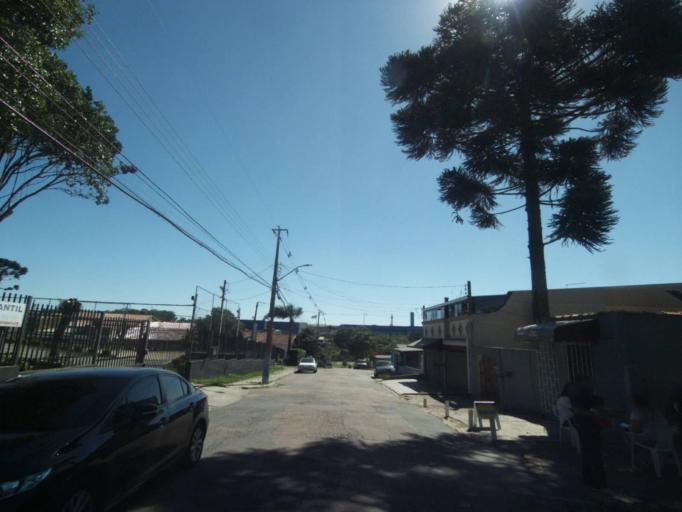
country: BR
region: Parana
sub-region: Curitiba
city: Curitiba
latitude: -25.4538
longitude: -49.3547
